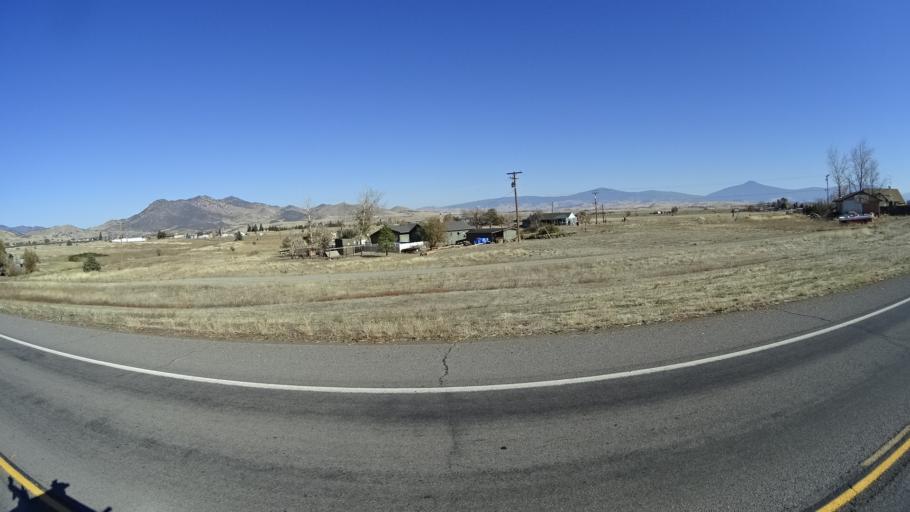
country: US
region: California
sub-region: Siskiyou County
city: Yreka
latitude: 41.7370
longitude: -122.5948
